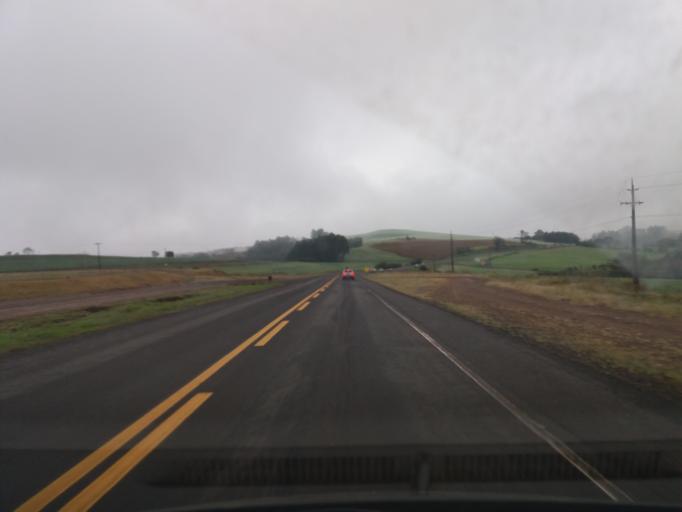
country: BR
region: Parana
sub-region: Realeza
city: Realeza
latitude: -25.8432
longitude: -53.5113
